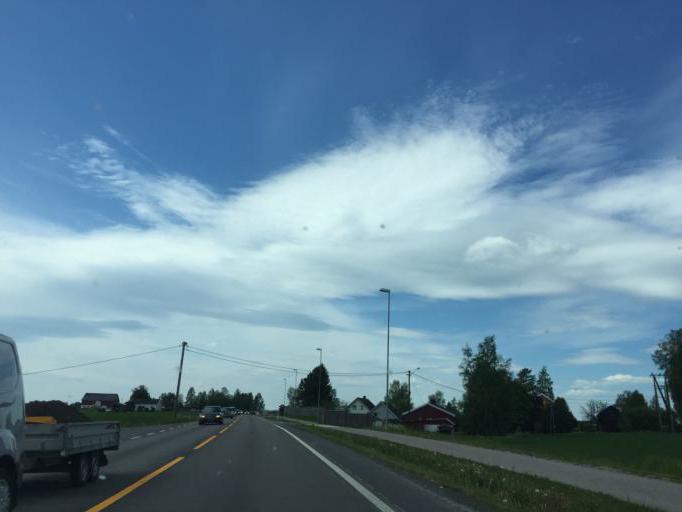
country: NO
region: Akershus
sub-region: Nes
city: Arnes
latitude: 60.1748
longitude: 11.4960
